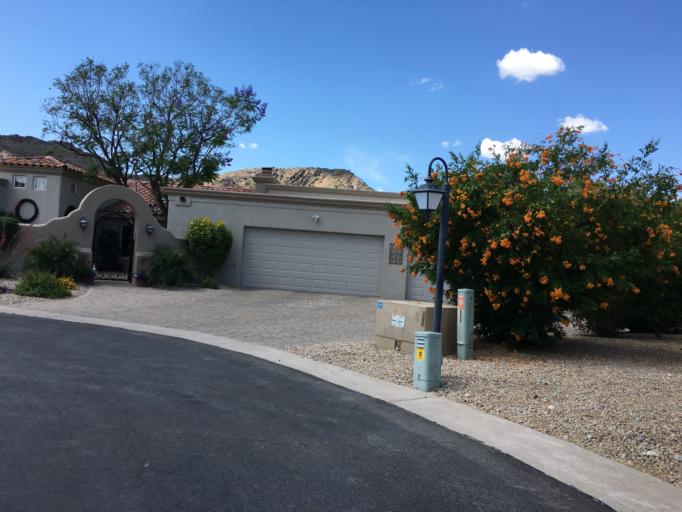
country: US
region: Arizona
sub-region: Maricopa County
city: Paradise Valley
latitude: 33.5755
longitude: -111.9882
